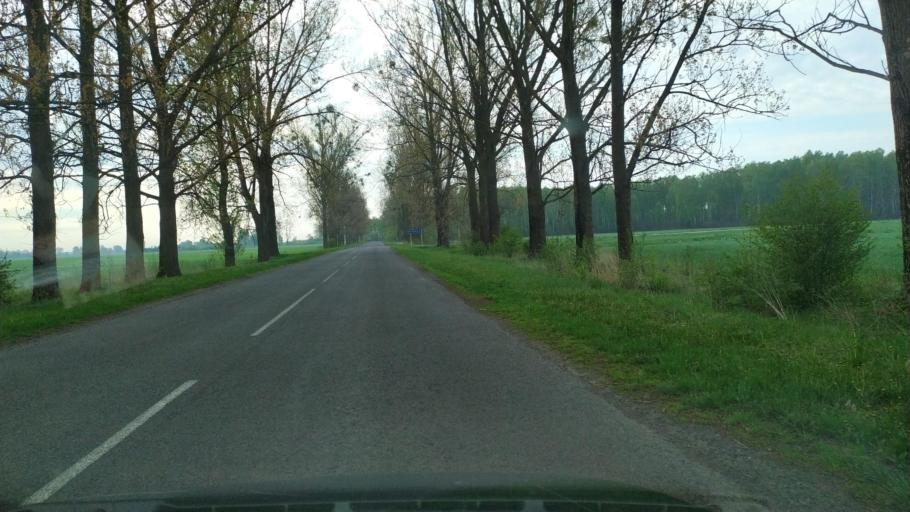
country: BY
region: Brest
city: Zhabinka
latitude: 52.1547
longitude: 24.0987
